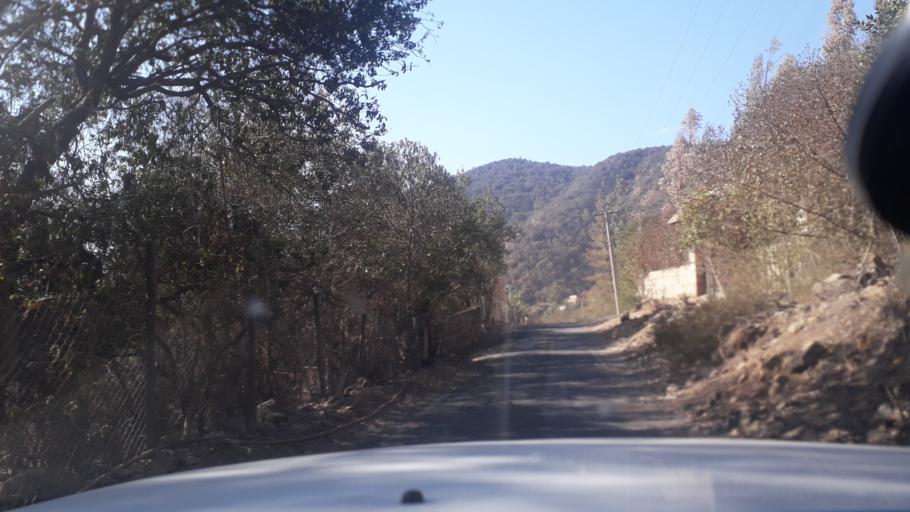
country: CL
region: Valparaiso
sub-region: Provincia de Marga Marga
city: Limache
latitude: -33.0677
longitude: -71.0972
